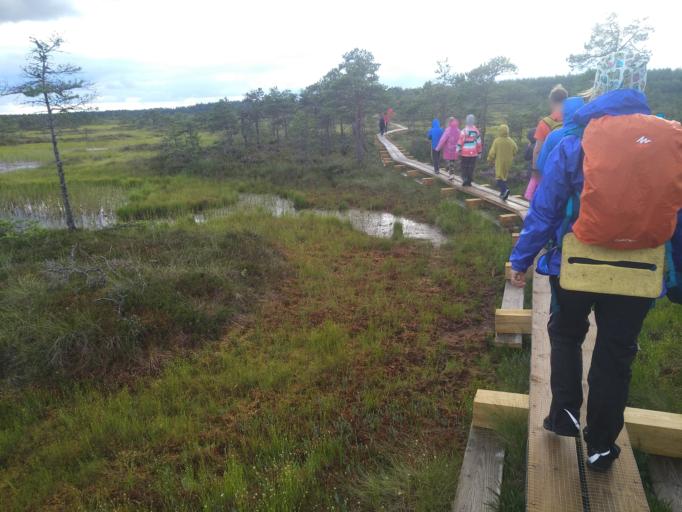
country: EE
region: Harju
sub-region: Anija vald
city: Kehra
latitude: 59.1897
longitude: 25.5244
